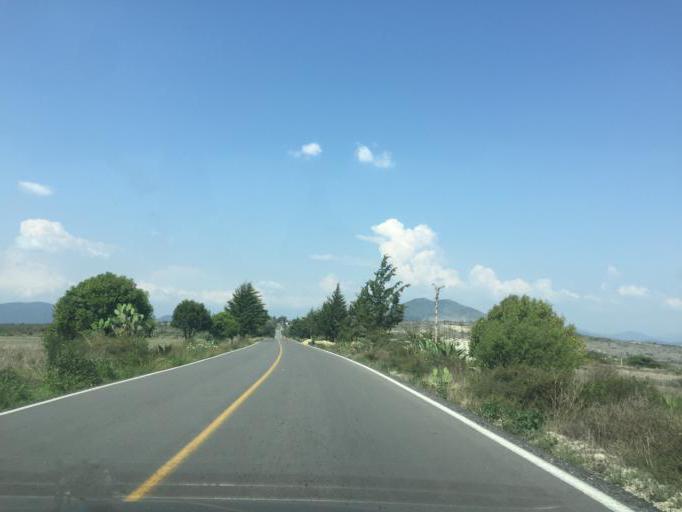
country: MX
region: Hidalgo
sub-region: Cardonal
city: Pozuelos
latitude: 20.6143
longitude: -99.0559
